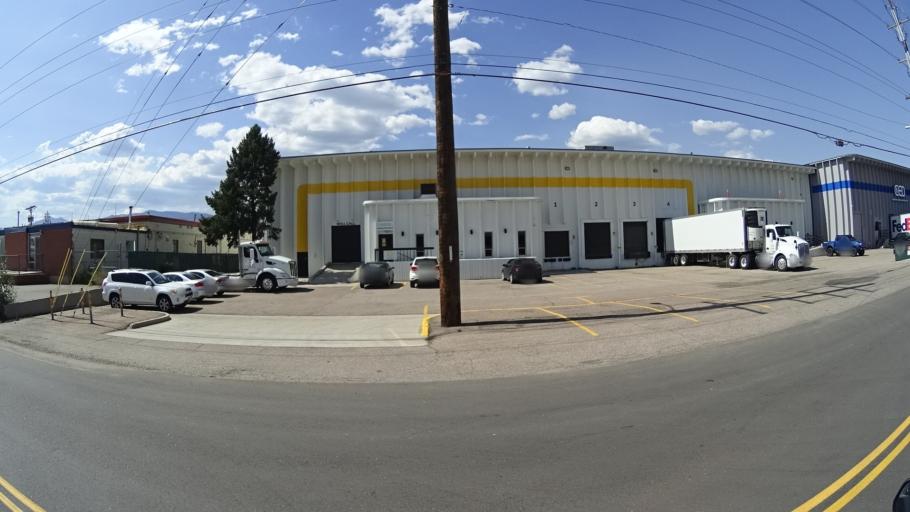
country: US
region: Colorado
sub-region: El Paso County
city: Colorado Springs
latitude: 38.8835
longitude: -104.8158
